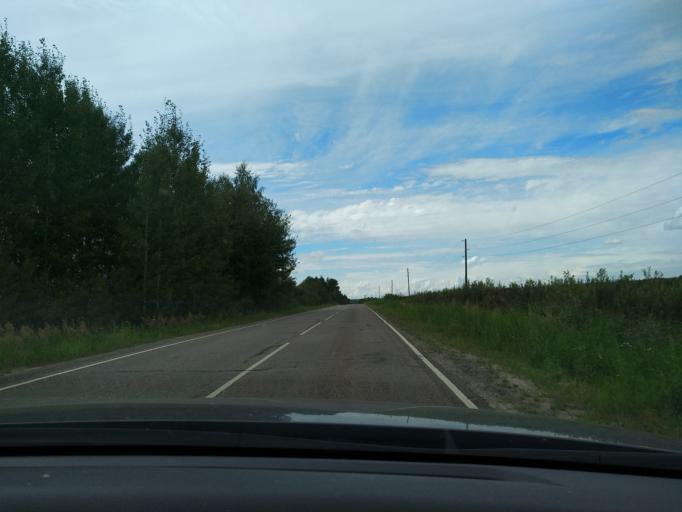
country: RU
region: Moskovskaya
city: Krasnyy Tkach
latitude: 55.3825
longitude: 39.1867
